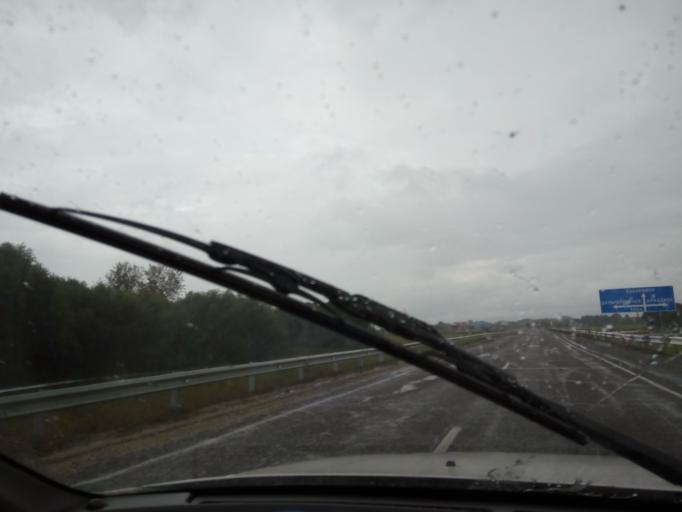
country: RU
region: Primorskiy
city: Dal'nerechensk
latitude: 45.9134
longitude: 133.7675
